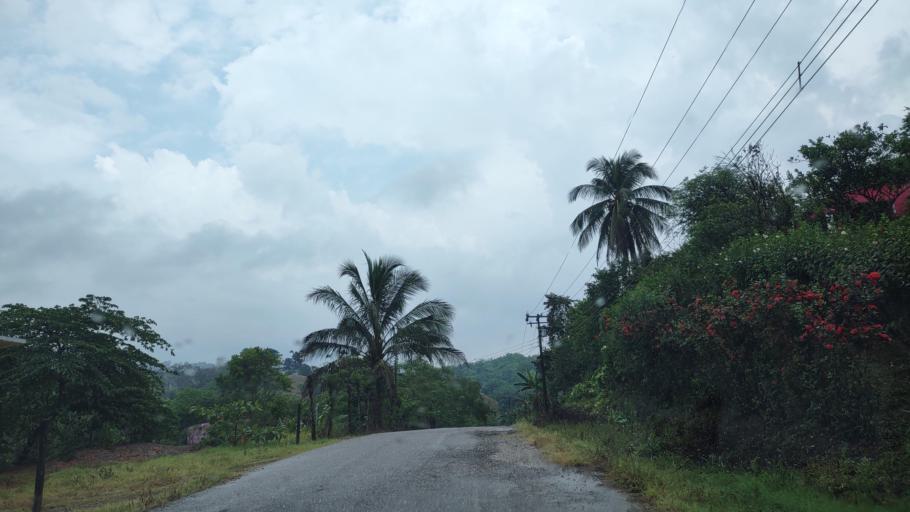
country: MX
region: Veracruz
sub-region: Uxpanapa
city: Poblado 10
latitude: 17.4708
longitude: -94.1191
